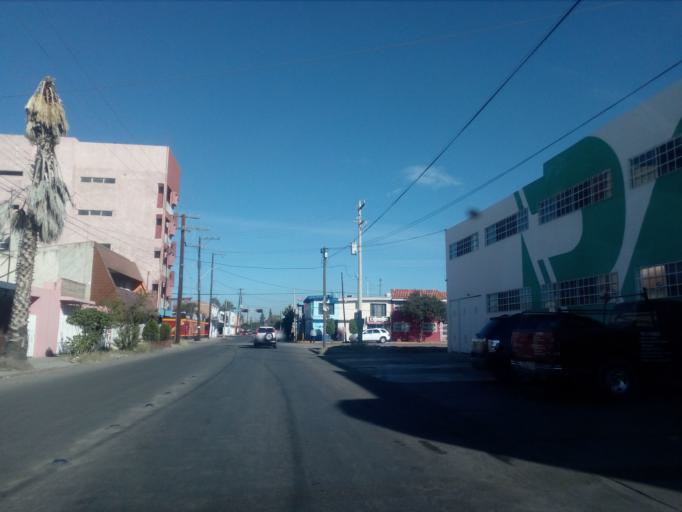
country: MX
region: Durango
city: Victoria de Durango
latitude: 24.0316
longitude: -104.6346
